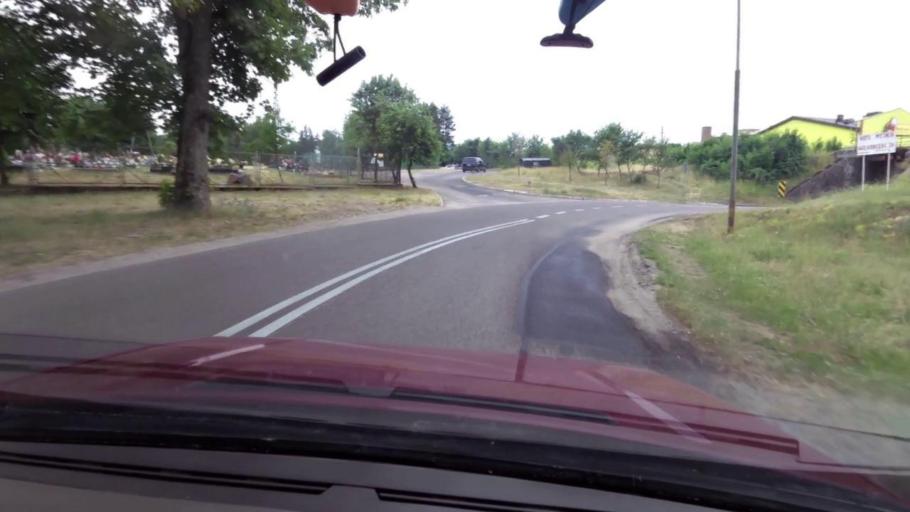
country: PL
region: Pomeranian Voivodeship
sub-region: Powiat slupski
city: Kepice
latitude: 54.2387
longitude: 16.8919
